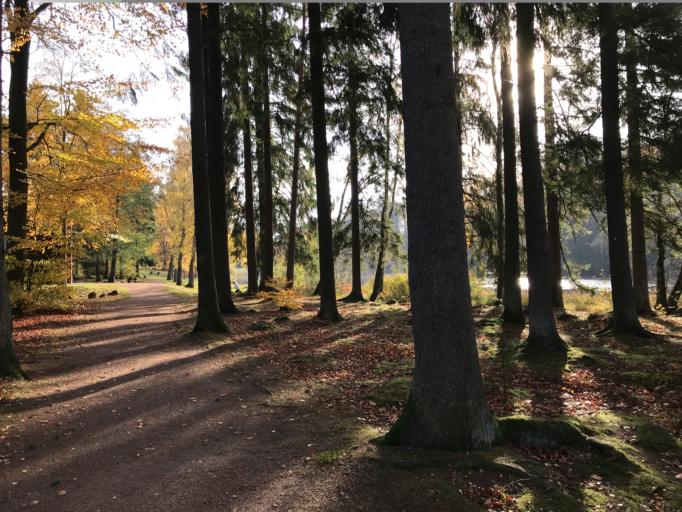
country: SE
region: Skane
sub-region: Svalovs Kommun
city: Kagerod
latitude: 56.0232
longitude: 13.1103
